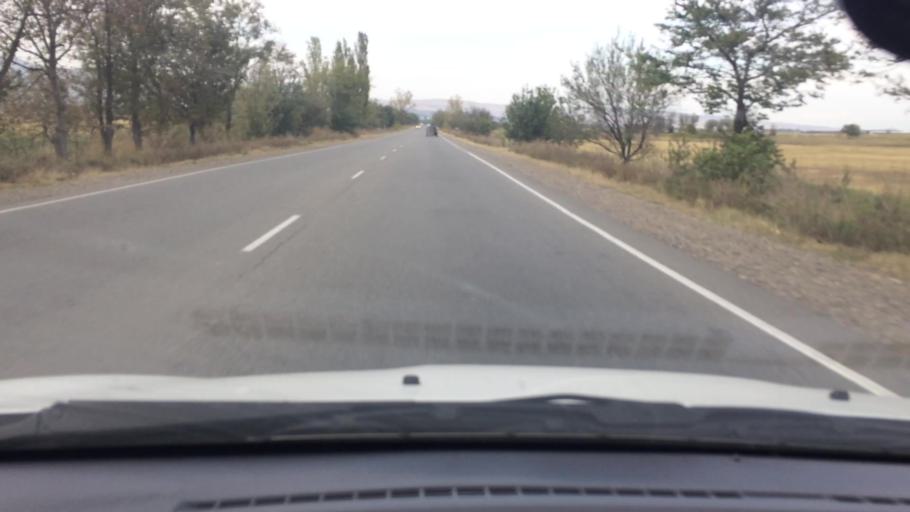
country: GE
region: Kvemo Kartli
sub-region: Marneuli
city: Marneuli
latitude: 41.5546
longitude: 44.7762
